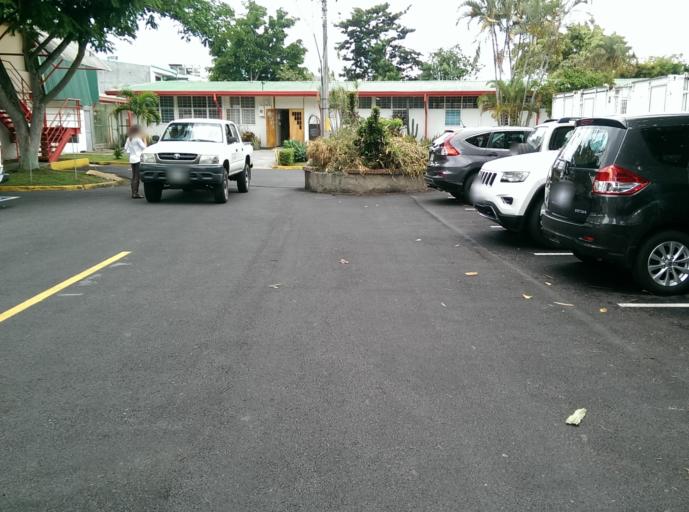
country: CR
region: San Jose
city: Sabanilla
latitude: 9.9399
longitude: -84.0484
